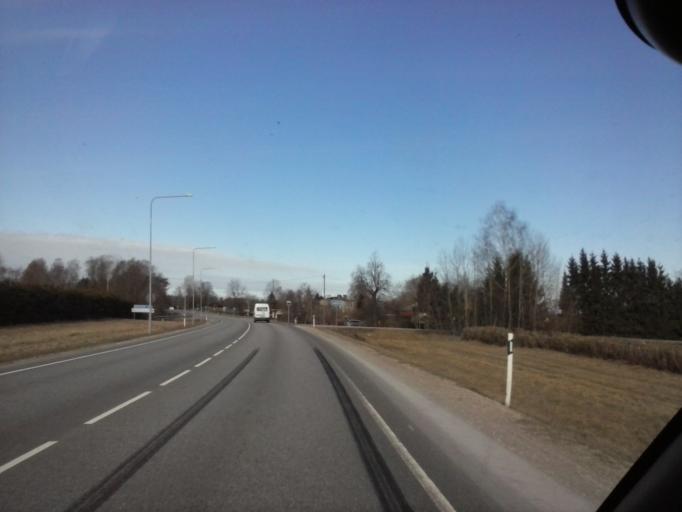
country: EE
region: Harju
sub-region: Anija vald
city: Kehra
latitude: 59.1022
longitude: 25.3652
